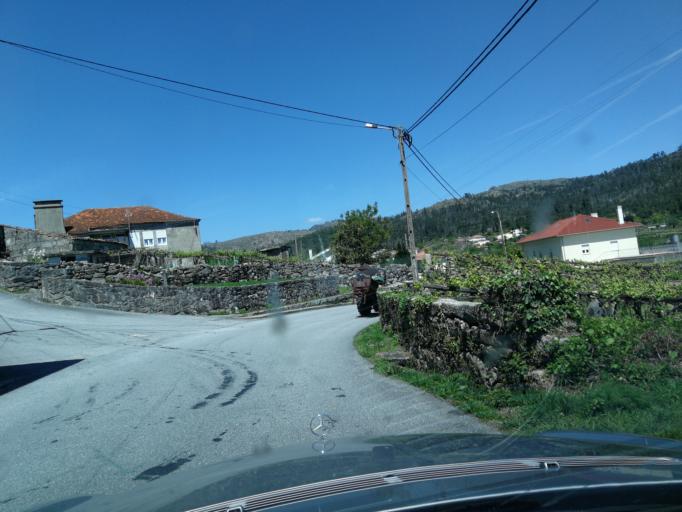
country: PT
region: Viana do Castelo
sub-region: Viana do Castelo
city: Meadela
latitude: 41.7422
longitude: -8.7830
